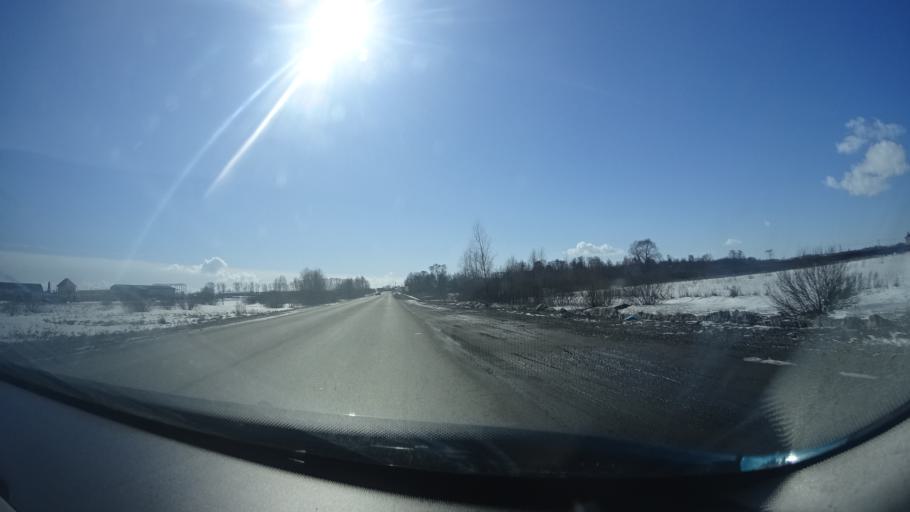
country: RU
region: Bashkortostan
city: Ufa
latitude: 54.6188
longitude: 55.8920
